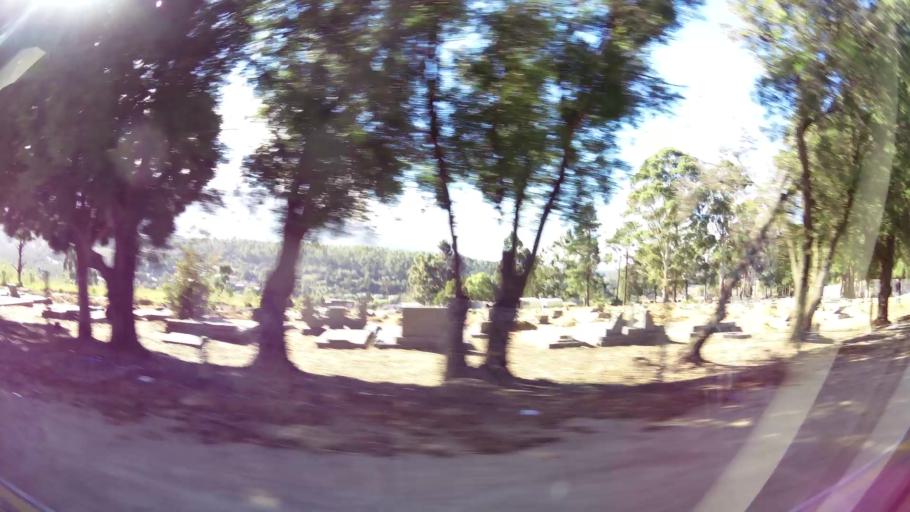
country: ZA
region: Western Cape
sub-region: Eden District Municipality
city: George
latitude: -33.9400
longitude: 22.4055
